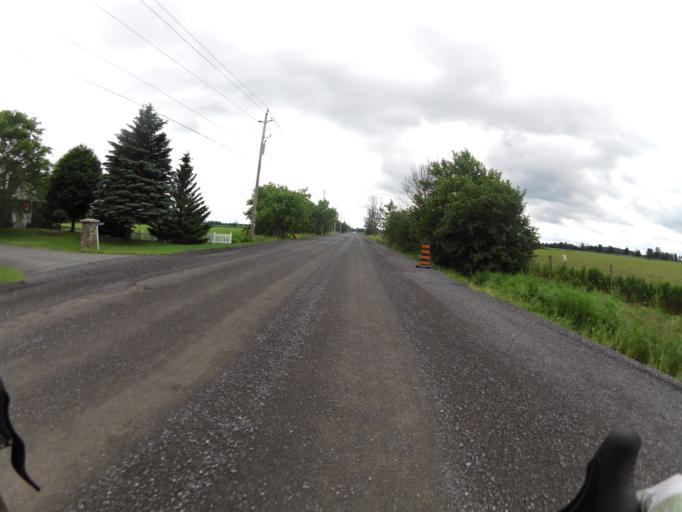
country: CA
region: Ontario
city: Bells Corners
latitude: 45.2162
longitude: -75.8472
